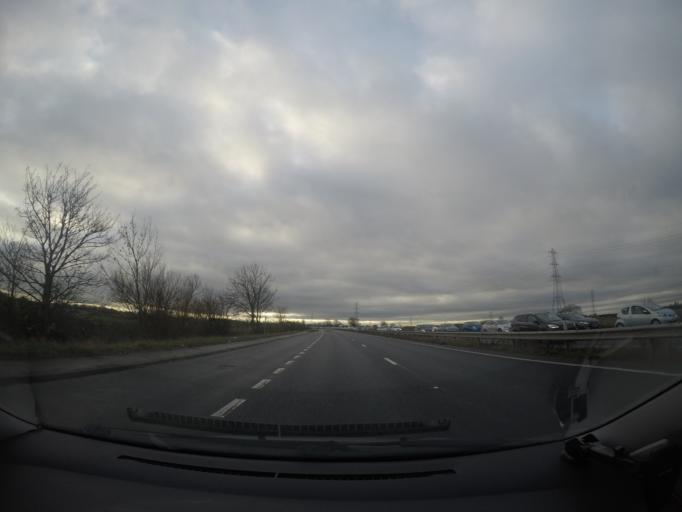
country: GB
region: England
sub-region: City of York
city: Murton
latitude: 53.9748
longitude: -1.0198
